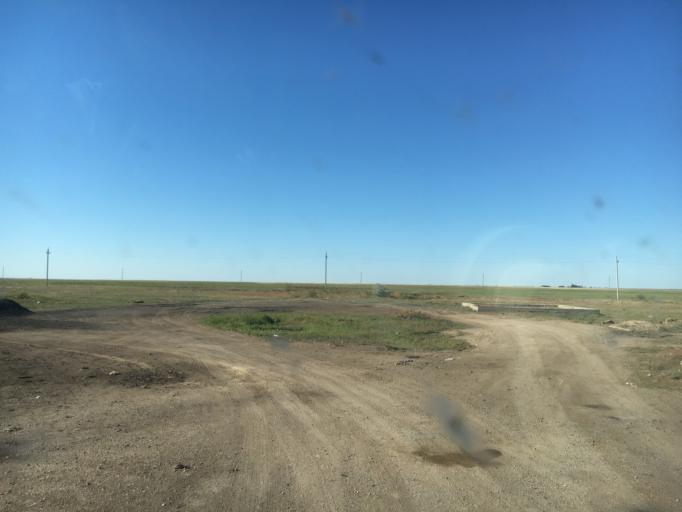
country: RU
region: Orenburg
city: Dombarovskiy
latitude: 50.1074
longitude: 59.3448
